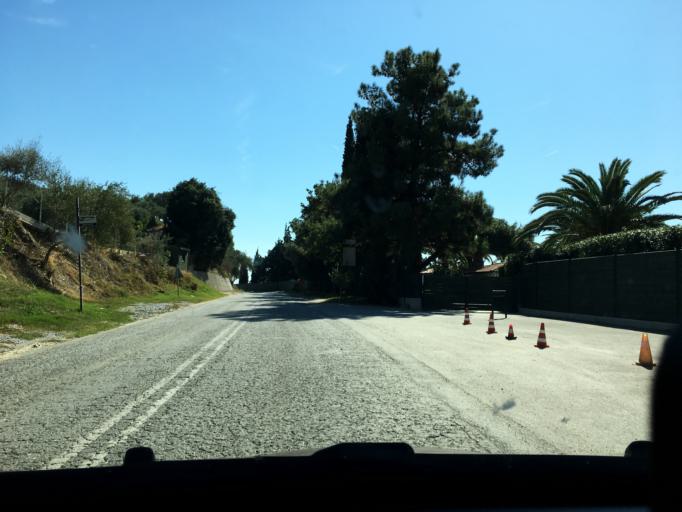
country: GR
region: Central Macedonia
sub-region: Nomos Chalkidikis
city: Ouranoupolis
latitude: 40.3540
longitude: 23.9518
